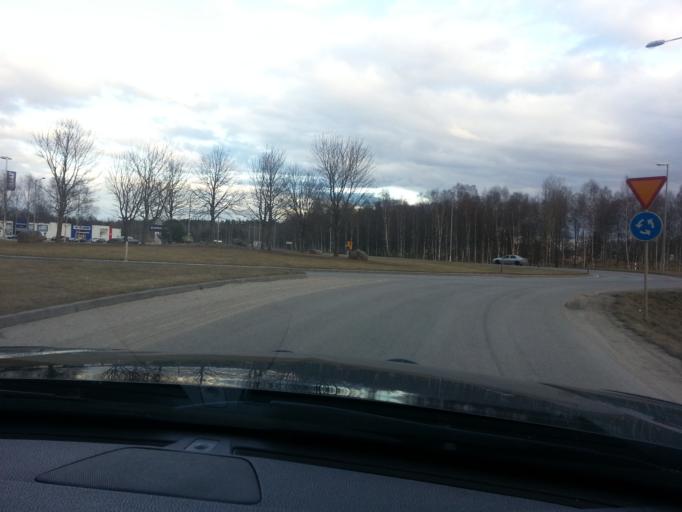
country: SE
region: Joenkoeping
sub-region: Vetlanda Kommun
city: Vetlanda
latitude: 57.4422
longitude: 15.0638
